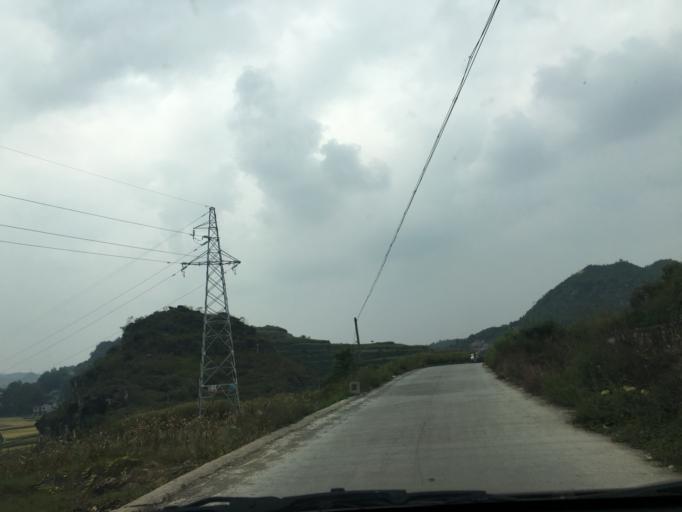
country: CN
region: Guangxi Zhuangzu Zizhiqu
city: Xinzhou
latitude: 25.5308
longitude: 105.6314
